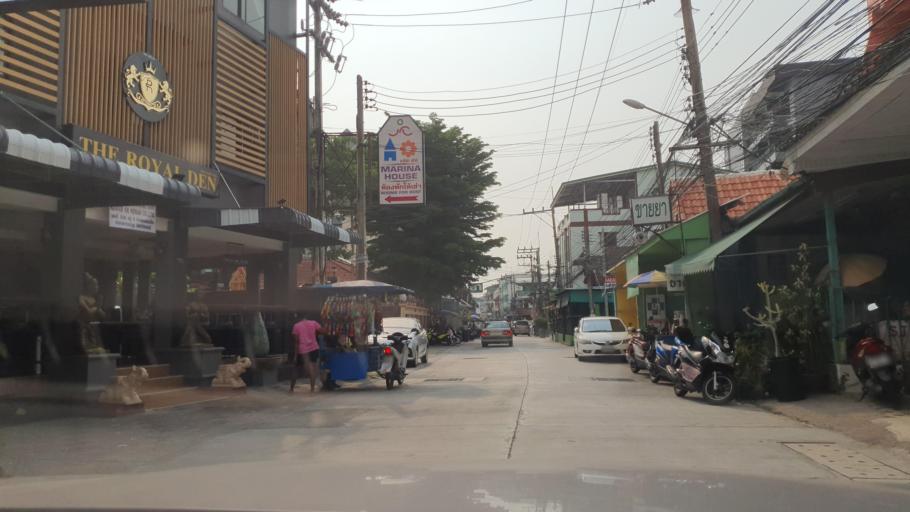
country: TH
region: Chon Buri
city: Phatthaya
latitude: 12.9308
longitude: 100.8892
